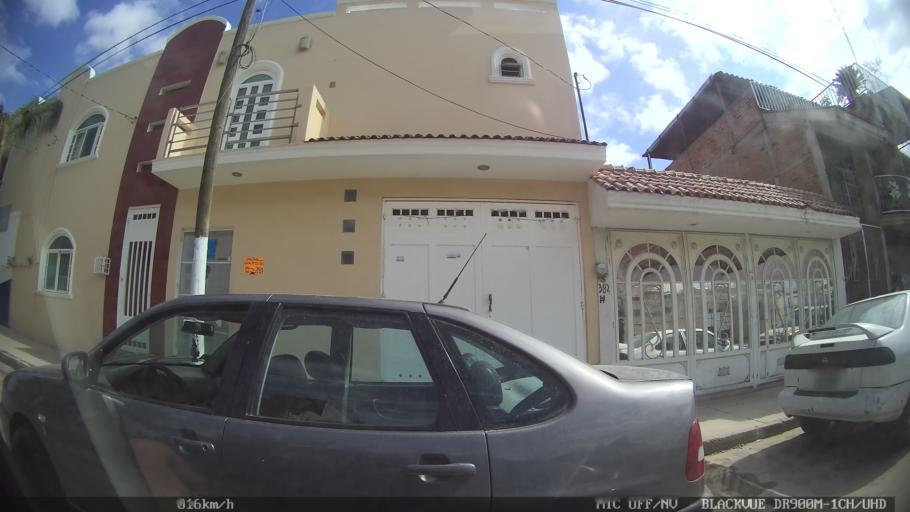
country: MX
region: Jalisco
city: Tonala
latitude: 20.6721
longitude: -103.2512
